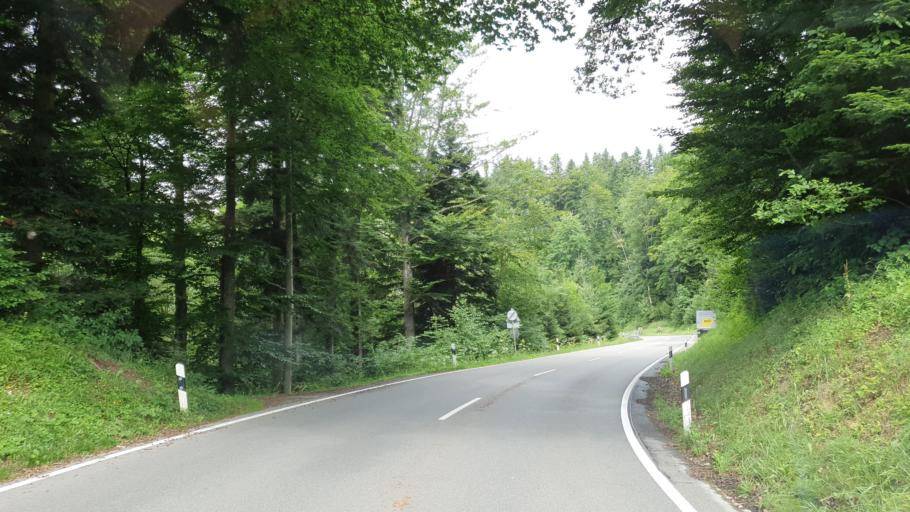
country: DE
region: Bavaria
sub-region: Swabia
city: Scheidegg
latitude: 47.5934
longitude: 9.8390
